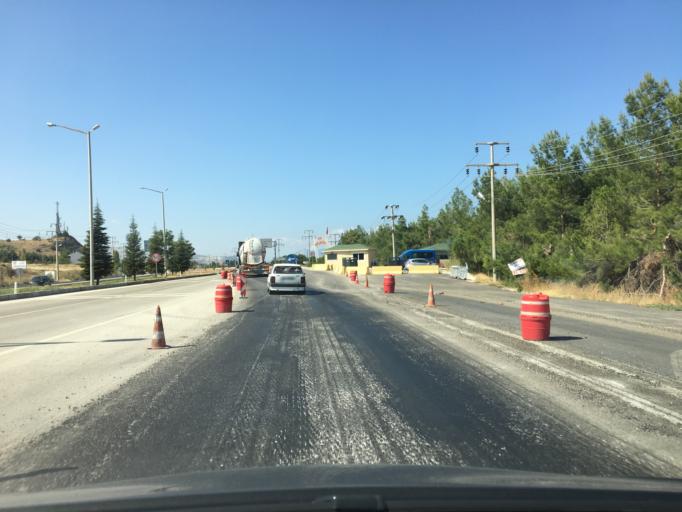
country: TR
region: Burdur
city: Burdur
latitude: 37.7486
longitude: 30.3232
